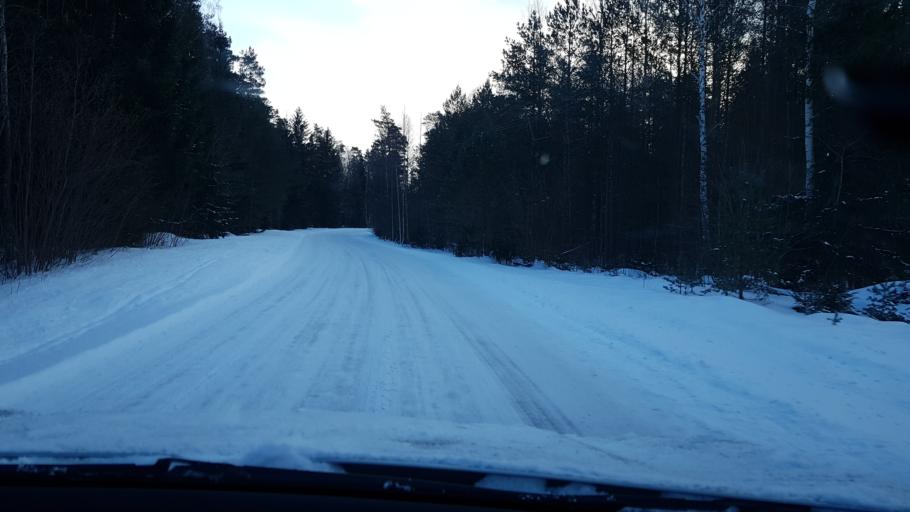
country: EE
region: Harju
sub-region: Nissi vald
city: Turba
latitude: 59.2184
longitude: 24.1399
